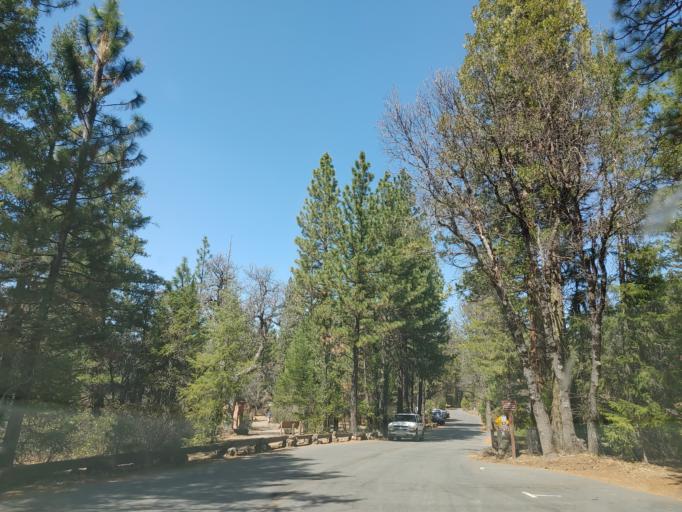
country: US
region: California
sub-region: Shasta County
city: Burney
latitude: 41.0120
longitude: -121.6506
